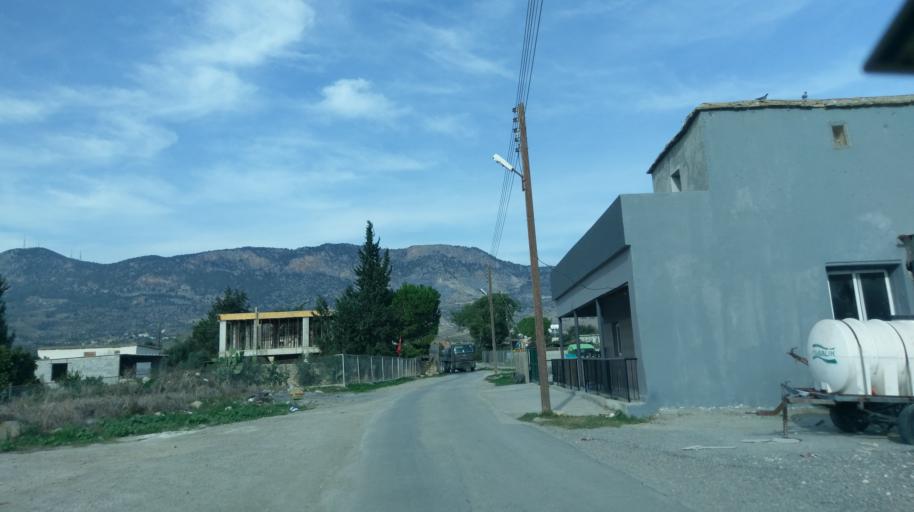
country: CY
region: Keryneia
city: Lapithos
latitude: 35.2790
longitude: 33.1729
